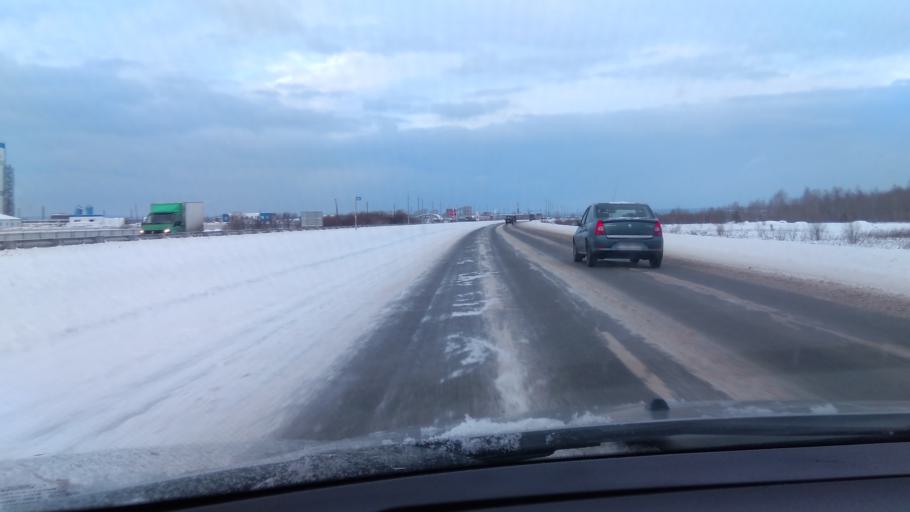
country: RU
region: Sverdlovsk
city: Tsementnyy
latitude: 57.4625
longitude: 60.1882
